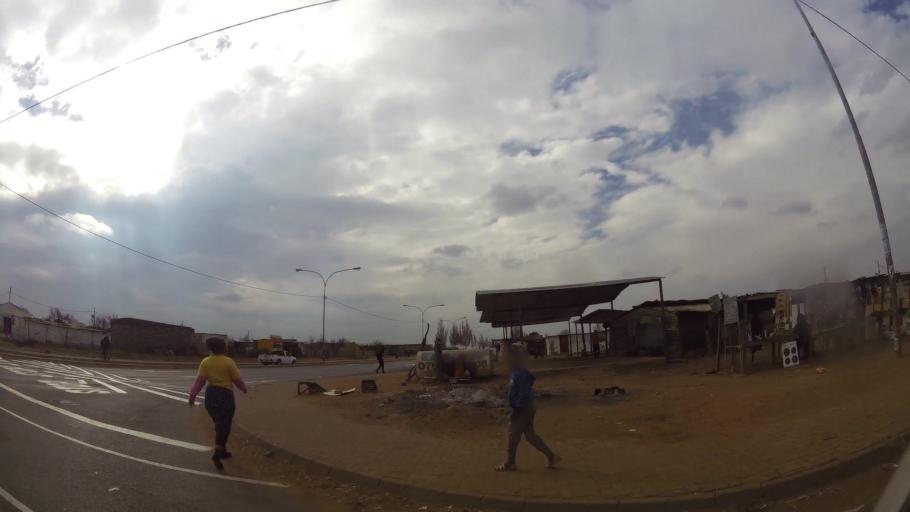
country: ZA
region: Gauteng
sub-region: Ekurhuleni Metropolitan Municipality
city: Germiston
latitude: -26.4015
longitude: 28.1558
